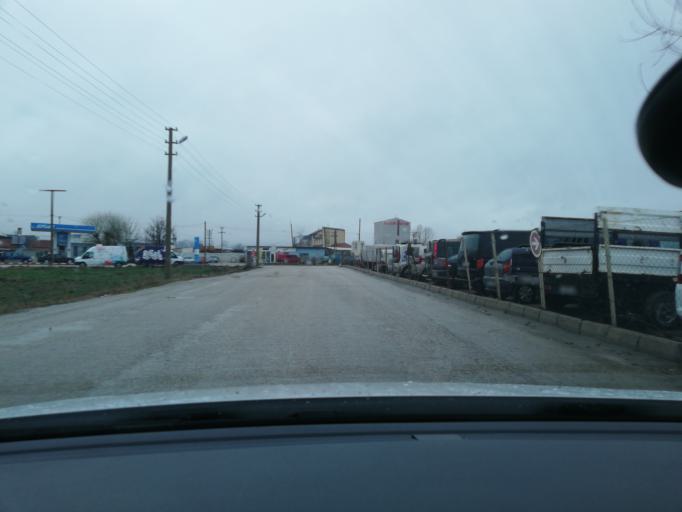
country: TR
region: Bolu
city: Bolu
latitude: 40.7374
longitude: 31.6327
